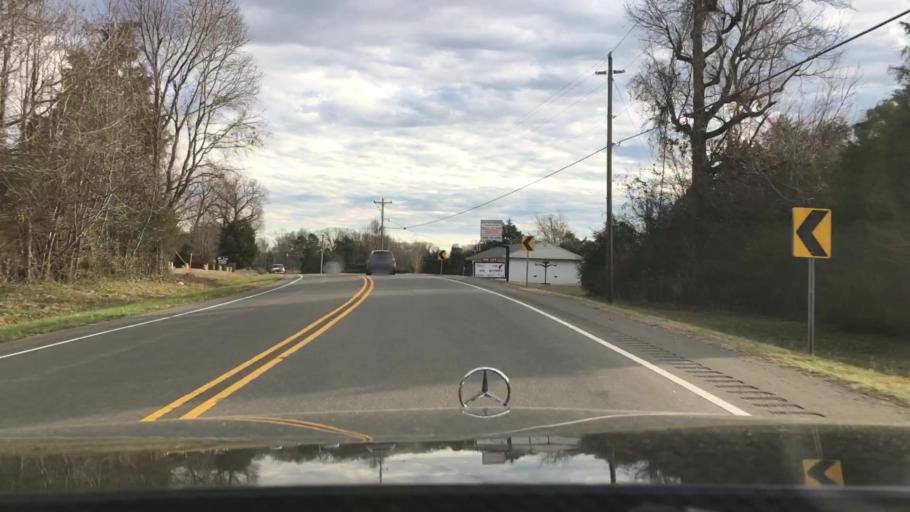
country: US
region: North Carolina
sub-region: Orange County
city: Hillsborough
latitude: 36.1591
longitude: -79.1296
